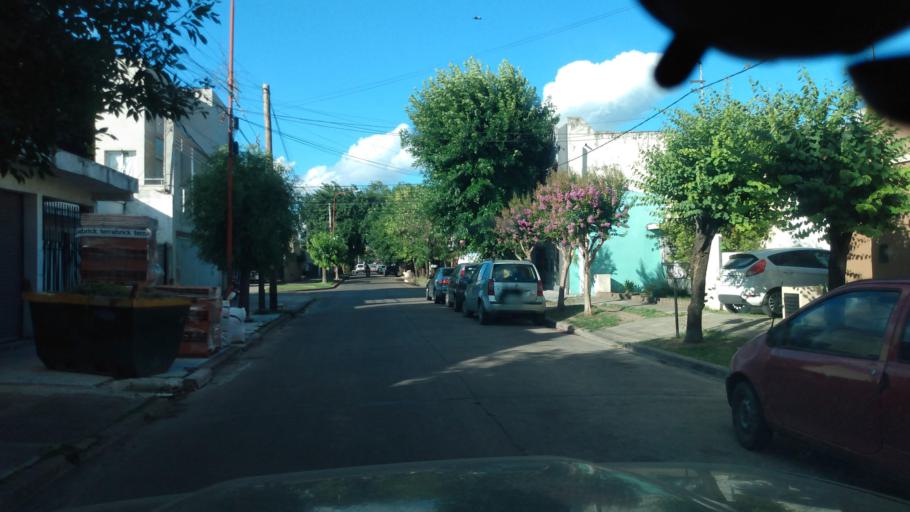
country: AR
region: Buenos Aires
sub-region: Partido de Lujan
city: Lujan
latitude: -34.5639
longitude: -59.1058
